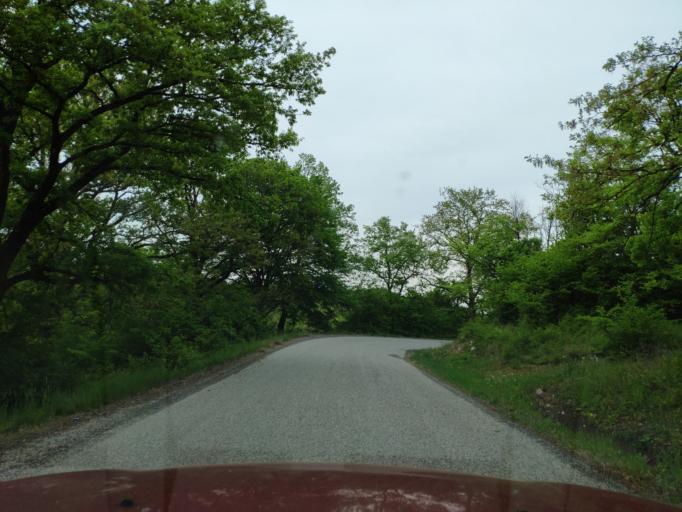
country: SK
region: Banskobystricky
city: Rimavska Sobota
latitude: 48.4969
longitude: 20.0952
